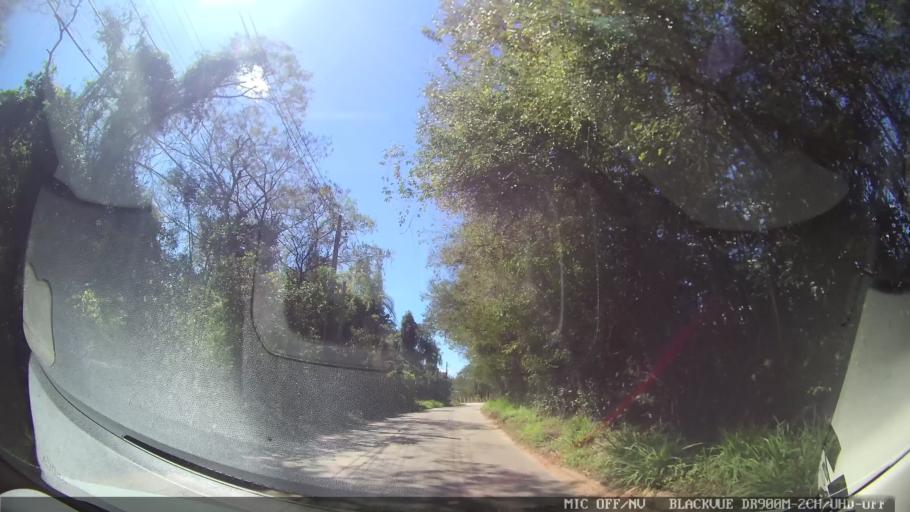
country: BR
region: Sao Paulo
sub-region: Jarinu
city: Jarinu
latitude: -23.1627
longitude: -46.7337
